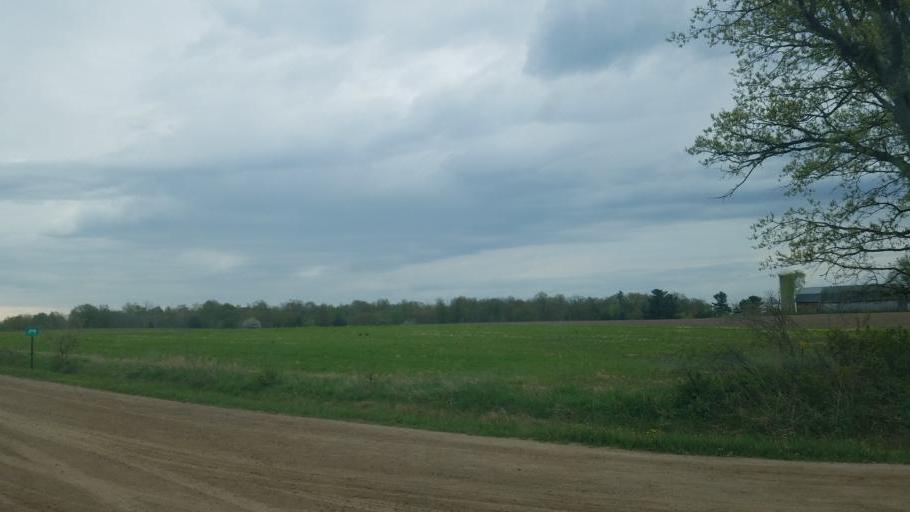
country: US
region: Wisconsin
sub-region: Clark County
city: Loyal
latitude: 44.6255
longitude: -90.4360
